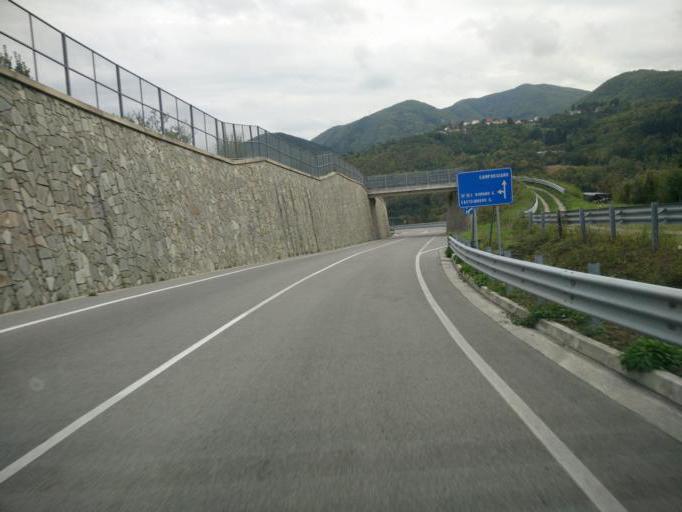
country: IT
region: Tuscany
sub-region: Provincia di Lucca
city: Piazza al Serchio-San Michele
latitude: 44.1799
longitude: 10.3099
